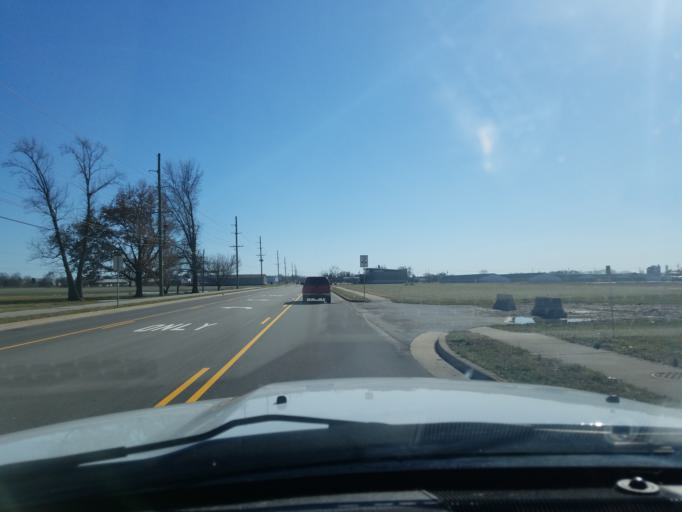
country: US
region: Indiana
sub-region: Shelby County
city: Shelbyville
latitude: 39.5204
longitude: -85.7427
